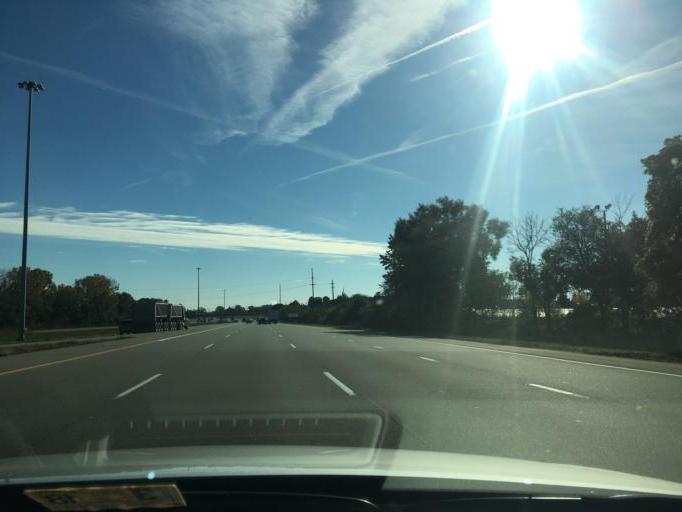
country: US
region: Michigan
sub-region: Wayne County
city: Plymouth
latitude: 42.3843
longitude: -83.4295
